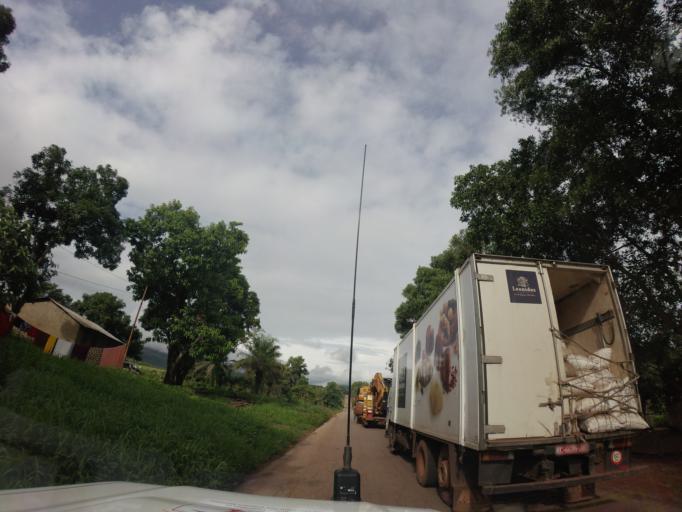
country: GN
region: Kindia
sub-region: Coyah
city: Coyah
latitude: 9.8102
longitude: -13.2734
